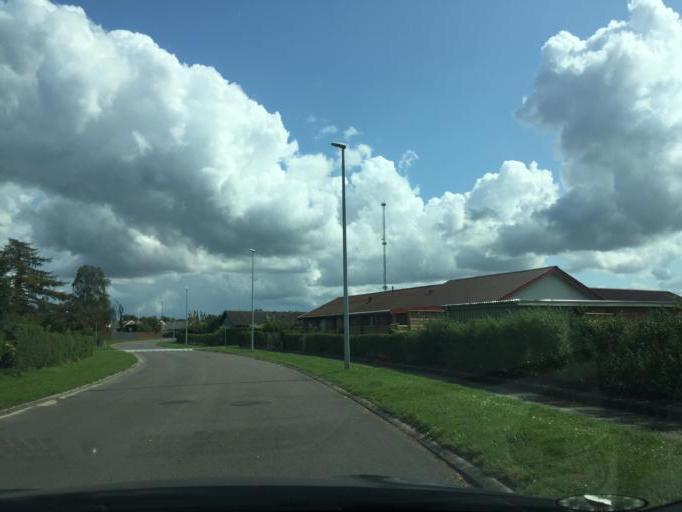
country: DK
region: South Denmark
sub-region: Odense Kommune
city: Neder Holluf
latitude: 55.3611
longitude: 10.4506
